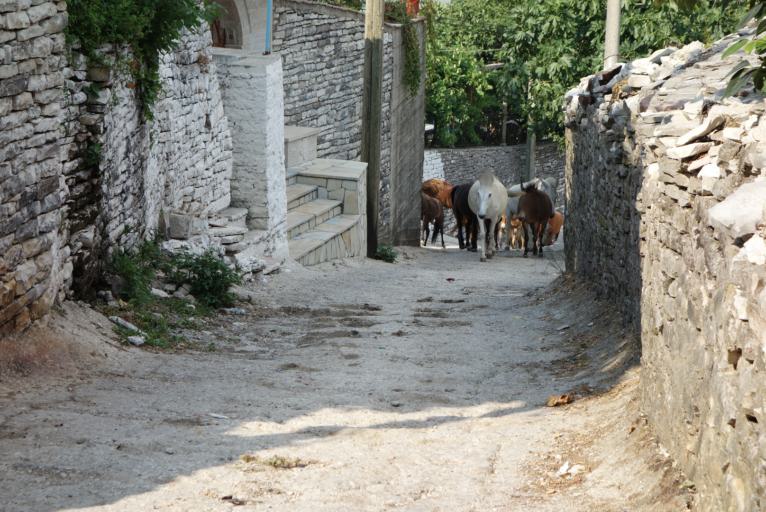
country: AL
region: Gjirokaster
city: Gjirokaster
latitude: 40.0701
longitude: 20.1323
